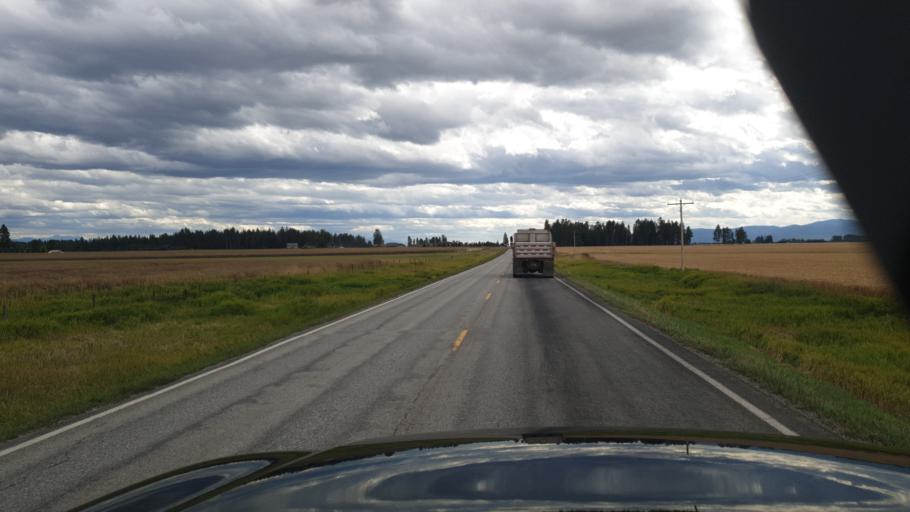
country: US
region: Montana
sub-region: Flathead County
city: Evergreen
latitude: 48.2460
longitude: -114.1652
